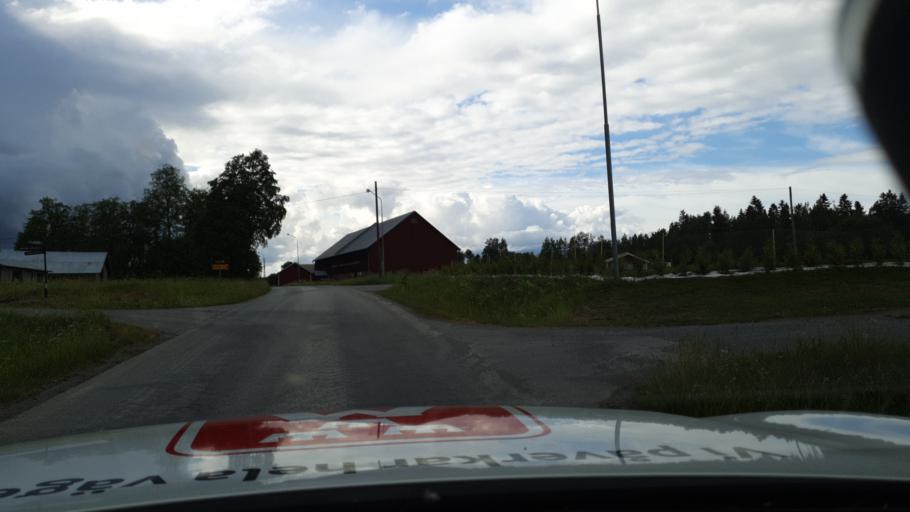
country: SE
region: Jaemtland
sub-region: OEstersunds Kommun
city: Ostersund
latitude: 63.0089
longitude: 14.6127
